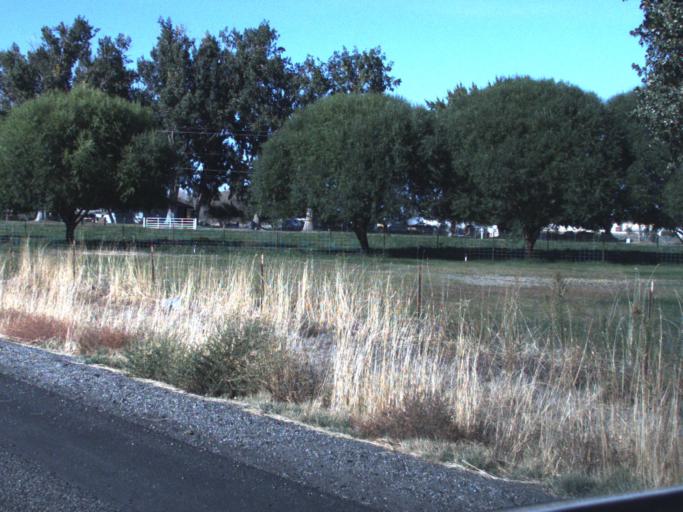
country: US
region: Washington
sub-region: Benton County
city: Finley
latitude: 46.1526
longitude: -119.0278
